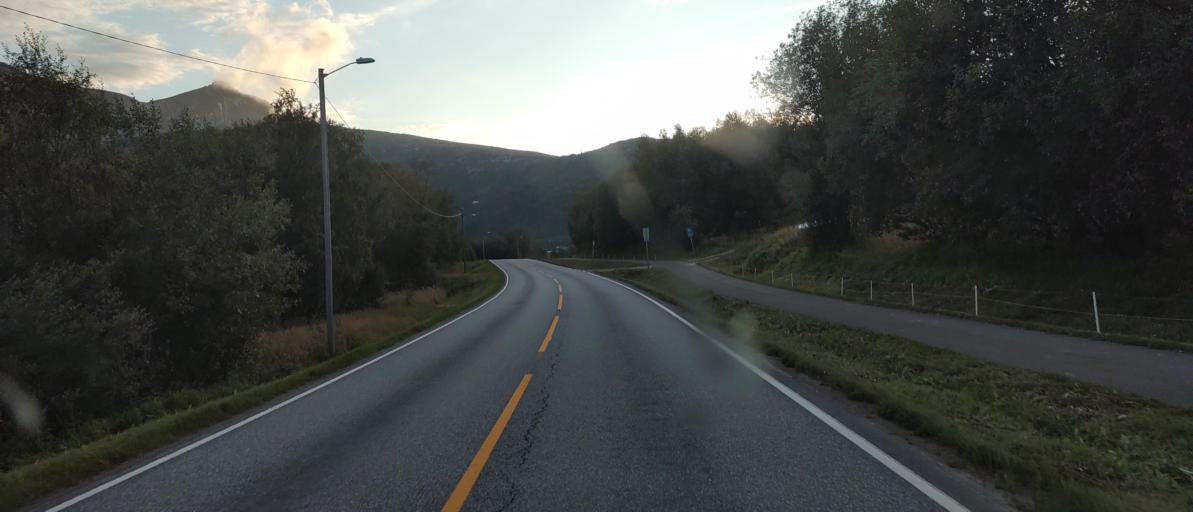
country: NO
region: Nordland
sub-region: Lodingen
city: Lodingen
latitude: 68.1934
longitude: 16.0465
